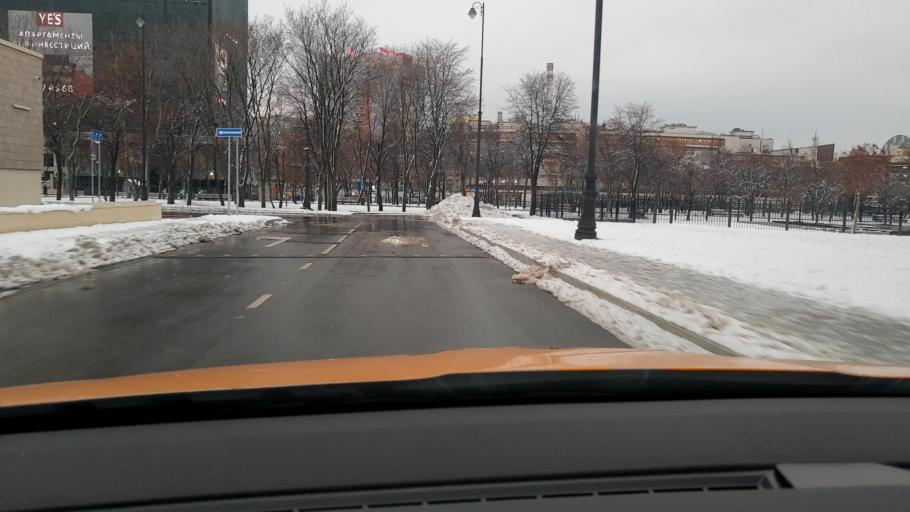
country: RU
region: Moskovskaya
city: Kozhukhovo
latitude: 55.6950
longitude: 37.6696
